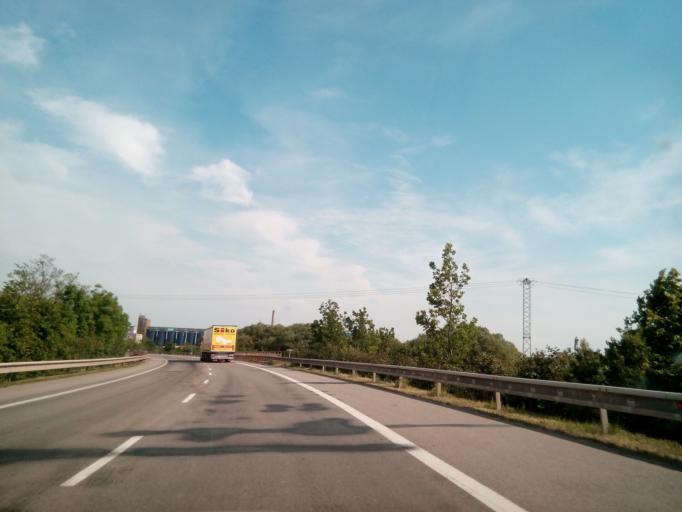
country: CZ
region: South Moravian
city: Slavkov u Brna
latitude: 49.1473
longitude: 16.8675
